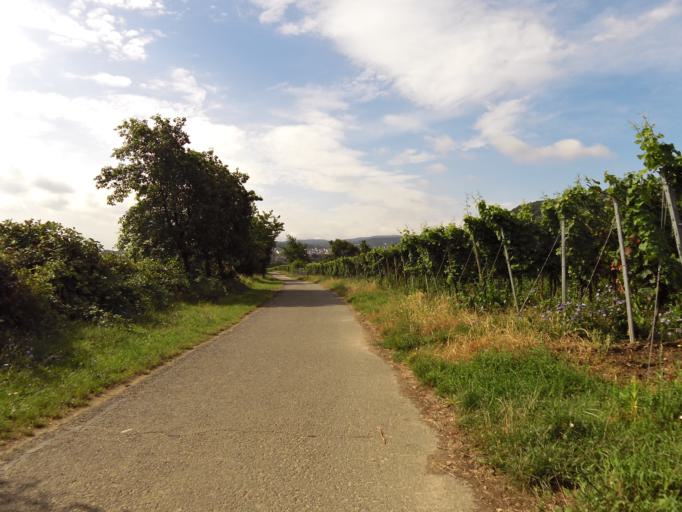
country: DE
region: Rheinland-Pfalz
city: Bad Duerkheim
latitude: 49.4726
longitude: 8.1663
